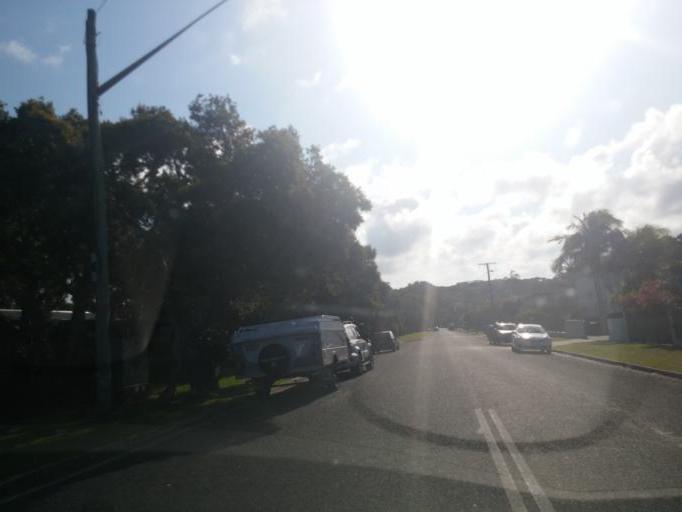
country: AU
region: New South Wales
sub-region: Coffs Harbour
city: Coffs Harbour
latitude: -30.2922
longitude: 153.1377
